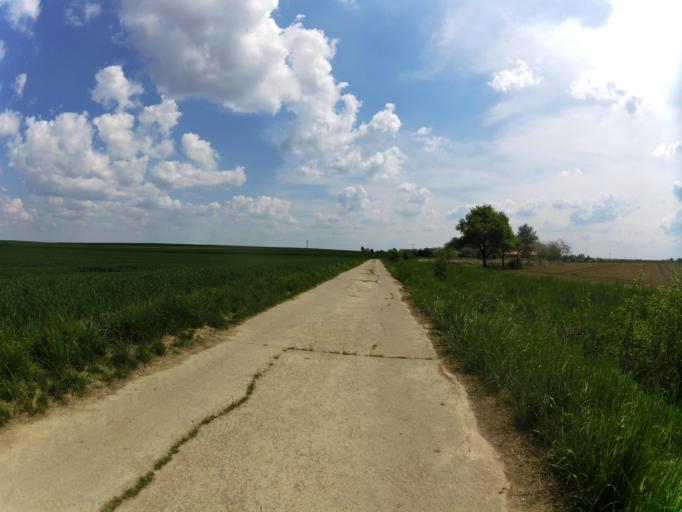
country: DE
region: Bavaria
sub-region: Regierungsbezirk Unterfranken
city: Giebelstadt
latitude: 49.6356
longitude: 9.9369
